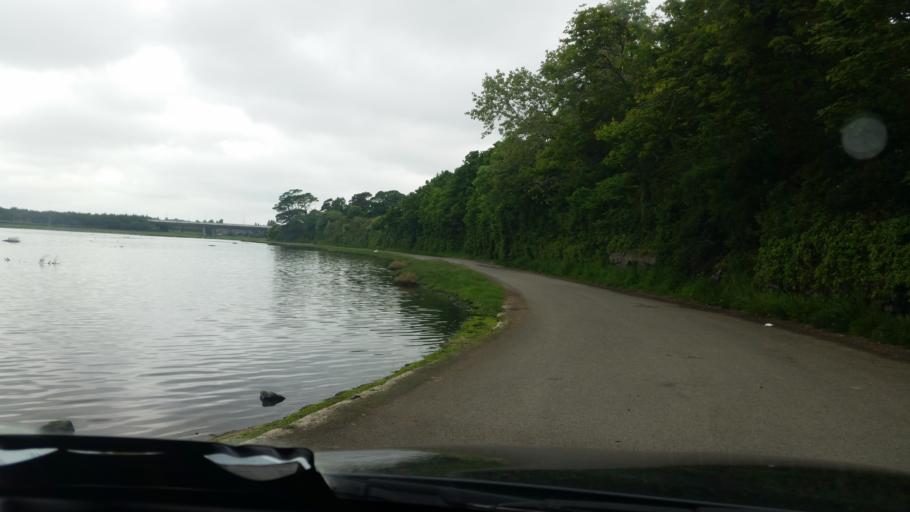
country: IE
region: Leinster
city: Kinsealy-Drinan
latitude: 53.4650
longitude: -6.1919
